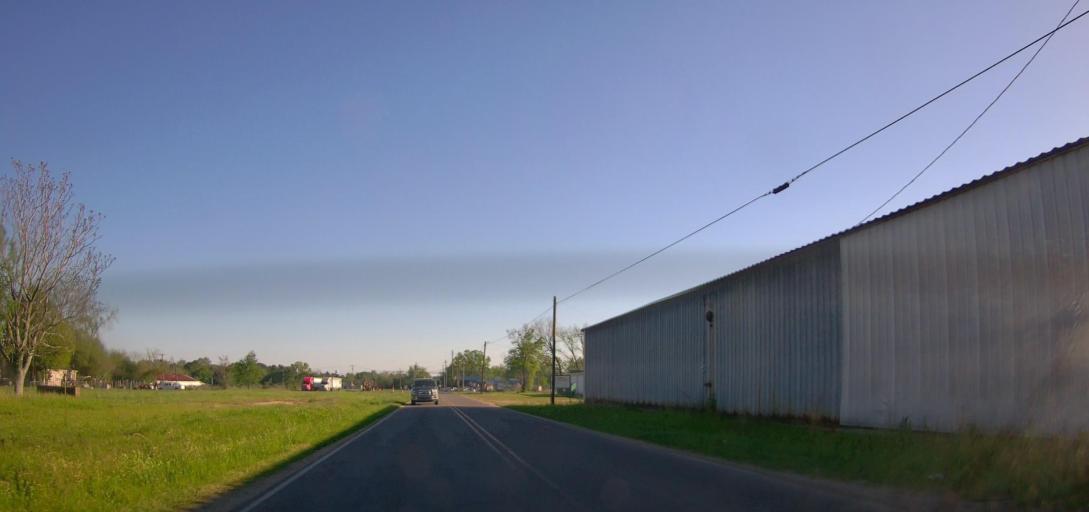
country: US
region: Georgia
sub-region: Ben Hill County
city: Fitzgerald
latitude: 31.7169
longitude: -83.2439
